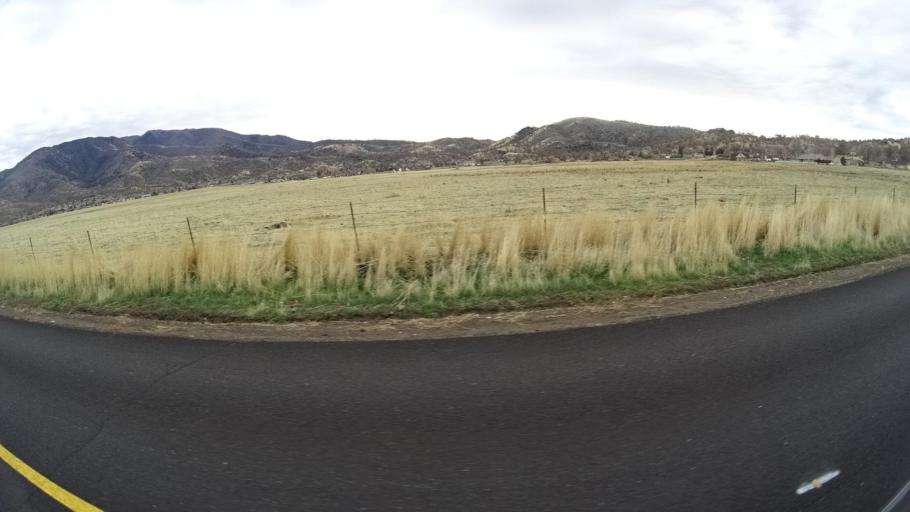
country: US
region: California
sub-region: Kern County
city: Stallion Springs
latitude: 35.0948
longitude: -118.6344
